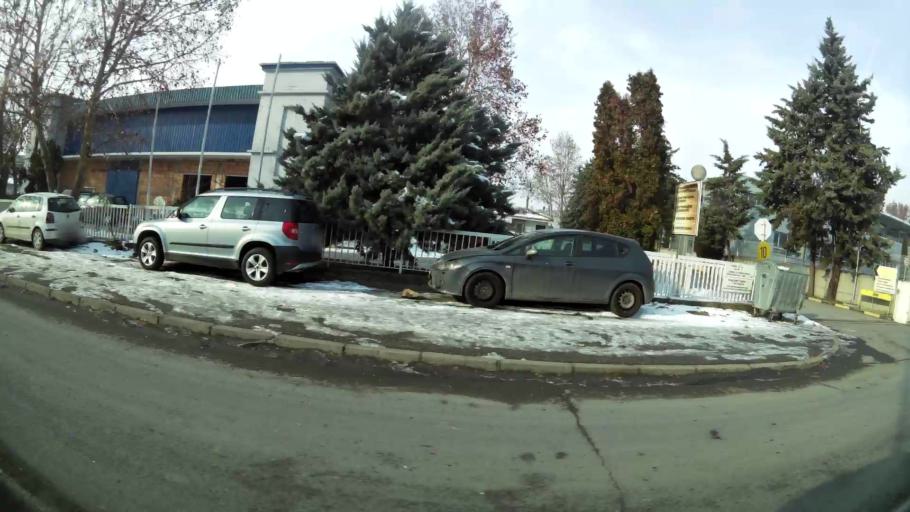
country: MK
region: Cair
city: Cair
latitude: 42.0244
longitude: 21.4341
